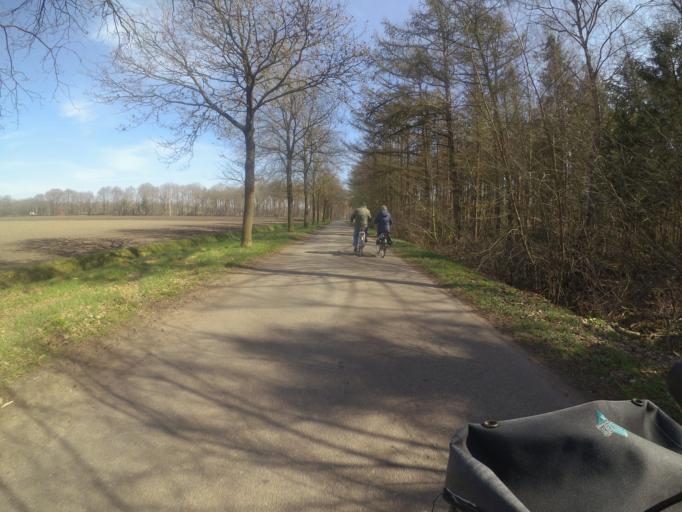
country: NL
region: North Brabant
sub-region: Gemeente Oirschot
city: Oirschot
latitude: 51.4900
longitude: 5.3102
